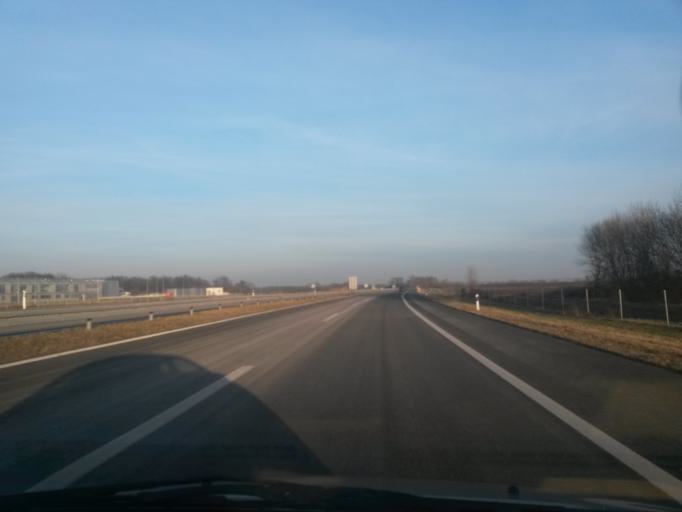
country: HR
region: Medimurska
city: Kursanec
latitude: 46.2679
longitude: 16.4109
